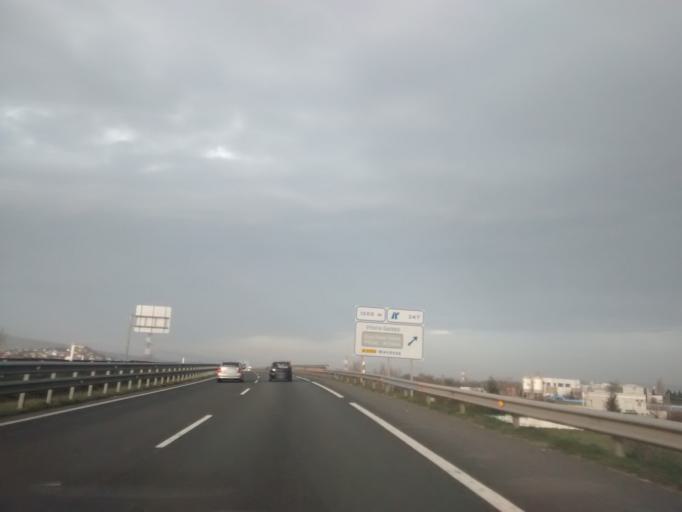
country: ES
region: Basque Country
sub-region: Provincia de Alava
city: Gasteiz / Vitoria
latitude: 42.8501
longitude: -2.7476
